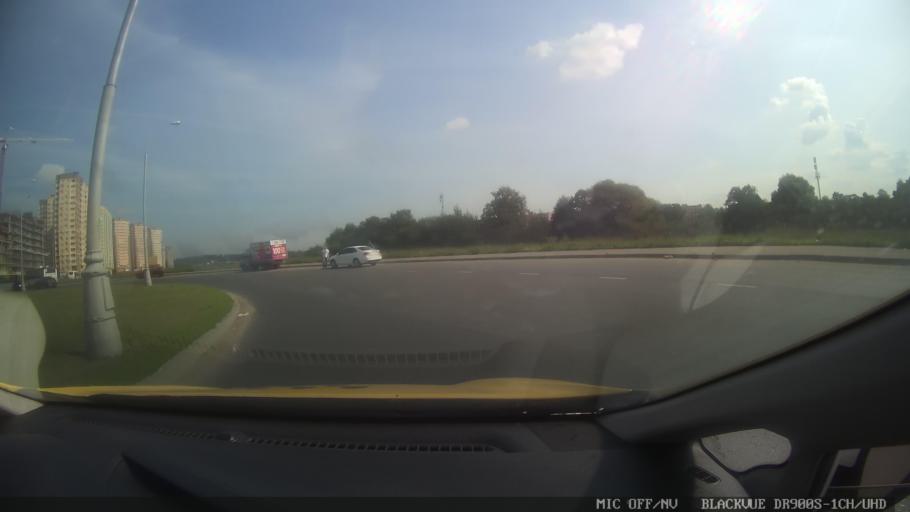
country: RU
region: Moskovskaya
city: Tomilino
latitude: 55.6937
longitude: 37.9595
